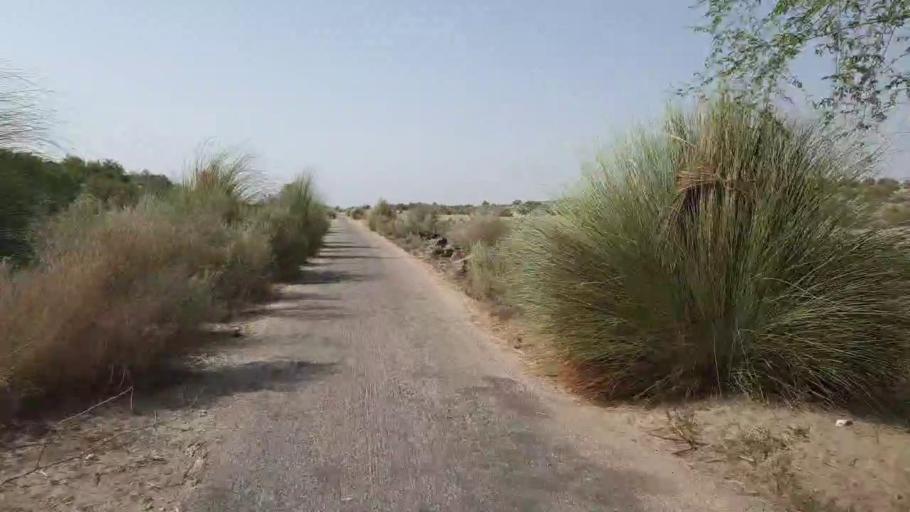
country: PK
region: Sindh
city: Jam Sahib
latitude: 26.5698
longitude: 68.9223
